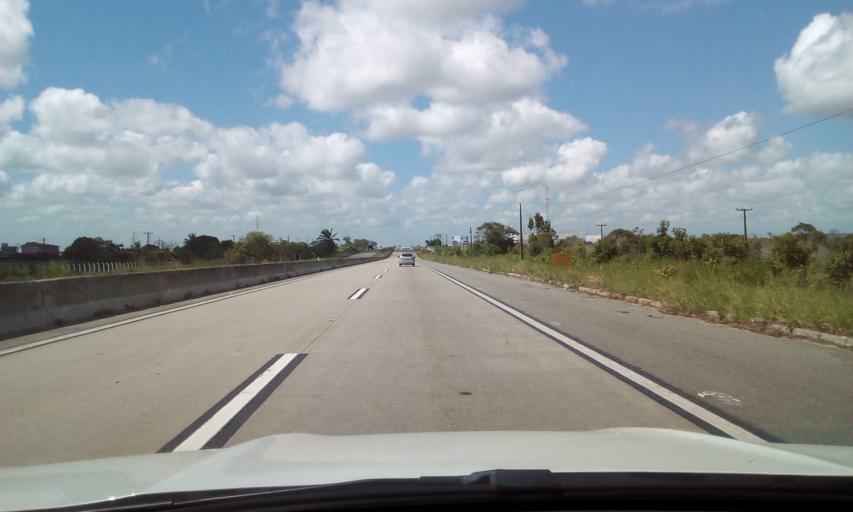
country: BR
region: Paraiba
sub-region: Conde
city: Conde
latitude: -7.2895
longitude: -34.9383
